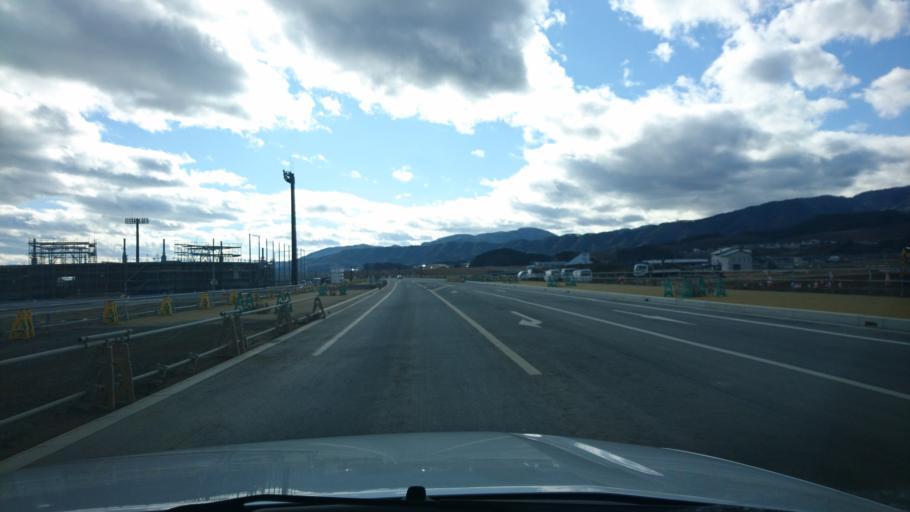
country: JP
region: Iwate
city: Ofunato
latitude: 39.0129
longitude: 141.6328
